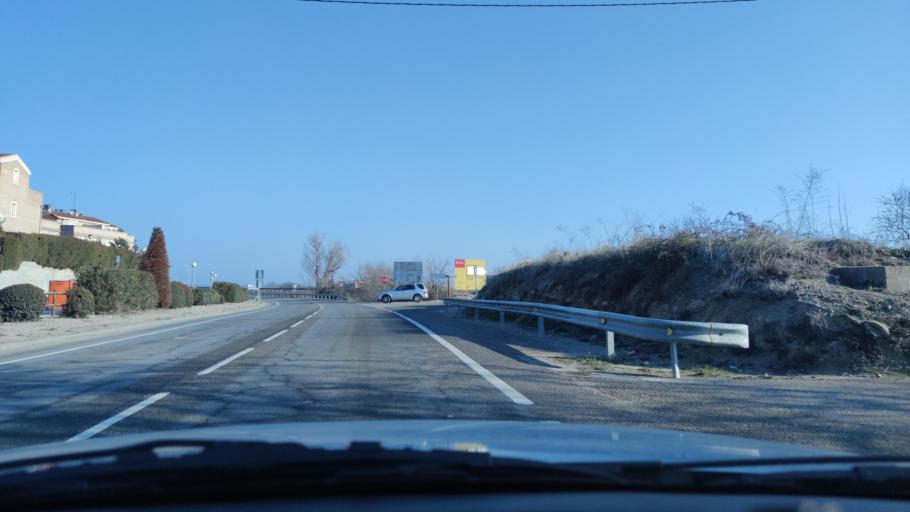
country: ES
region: Catalonia
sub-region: Provincia de Lleida
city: Torrefarrera
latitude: 41.6924
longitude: 0.6351
